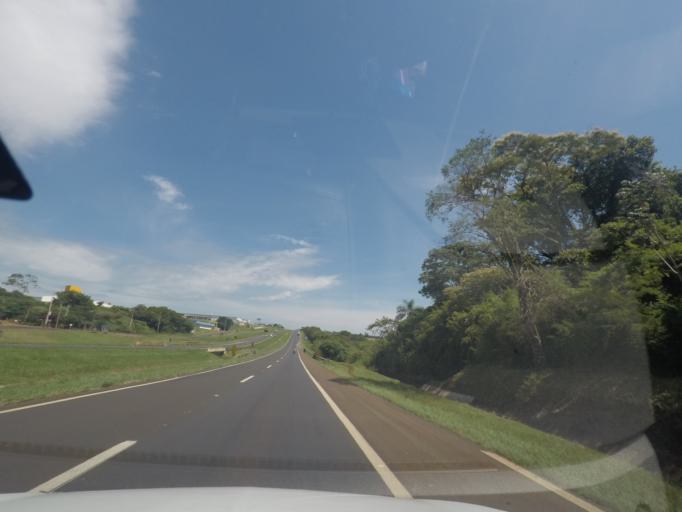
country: BR
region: Sao Paulo
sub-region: Araraquara
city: Araraquara
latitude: -21.7740
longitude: -48.2362
